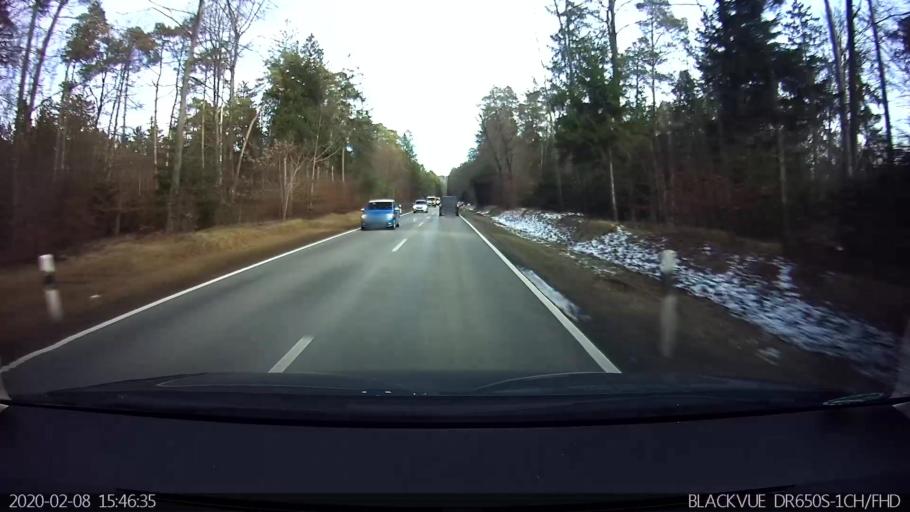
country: DE
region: Bavaria
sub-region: Upper Bavaria
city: Geretsried
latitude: 47.8594
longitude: 11.4948
